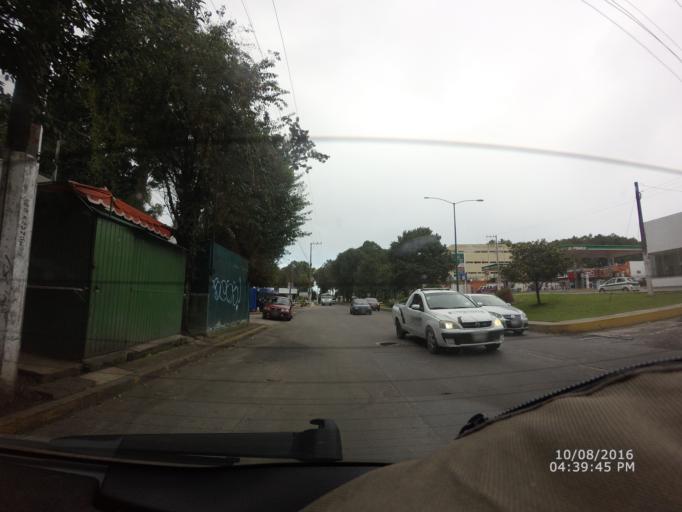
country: MX
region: Veracruz
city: Banderilla
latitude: 19.5625
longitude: -96.9303
